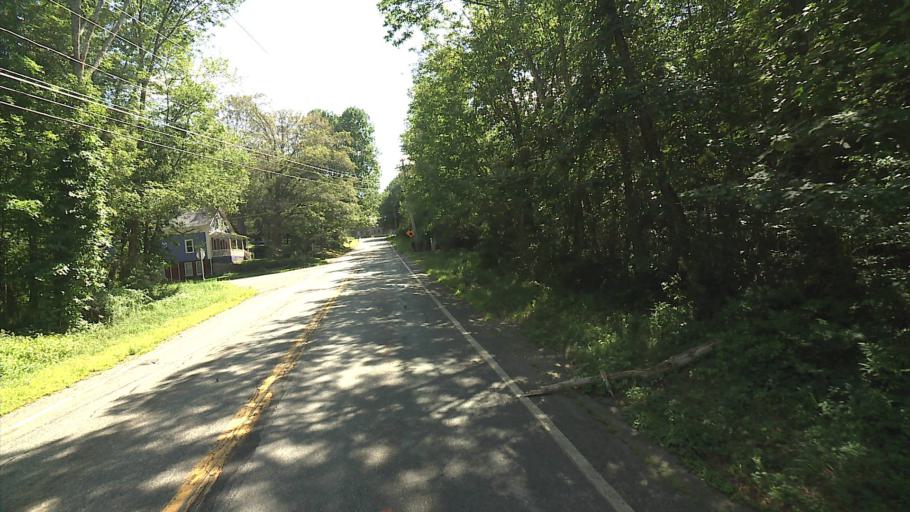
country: US
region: Connecticut
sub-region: Tolland County
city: Stafford
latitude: 41.9205
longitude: -72.1774
